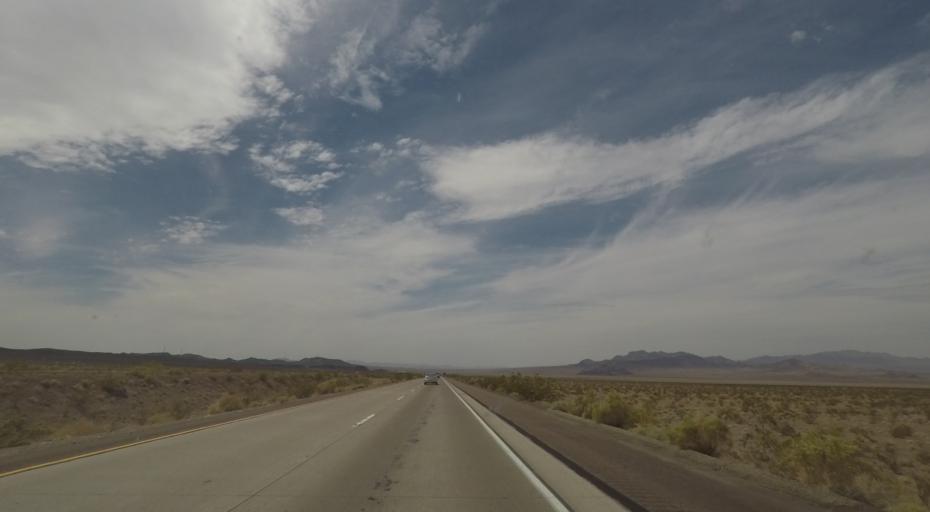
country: US
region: California
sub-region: San Bernardino County
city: Twentynine Palms
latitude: 34.7272
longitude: -116.1129
